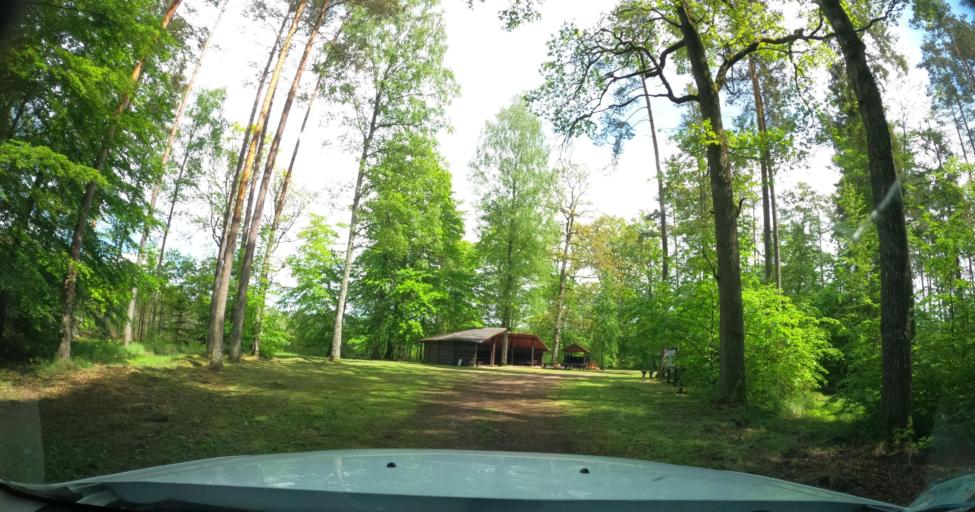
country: PL
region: Pomeranian Voivodeship
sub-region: Powiat slupski
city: Potegowo
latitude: 54.3940
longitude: 17.4749
